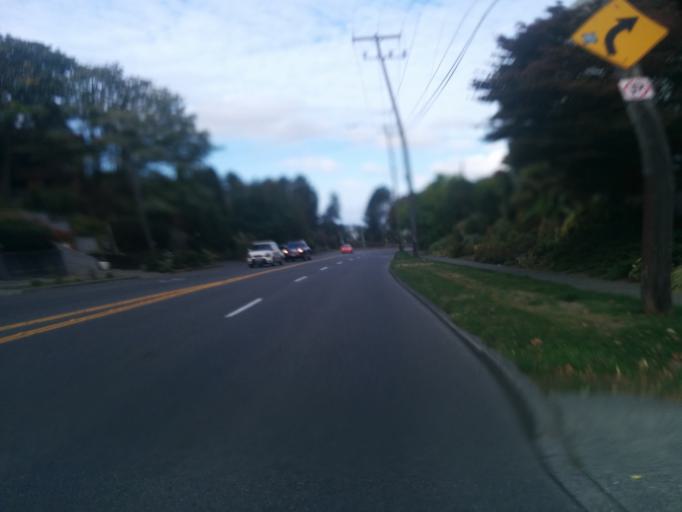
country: US
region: Washington
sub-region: King County
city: Shoreline
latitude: 47.6831
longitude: -122.3189
